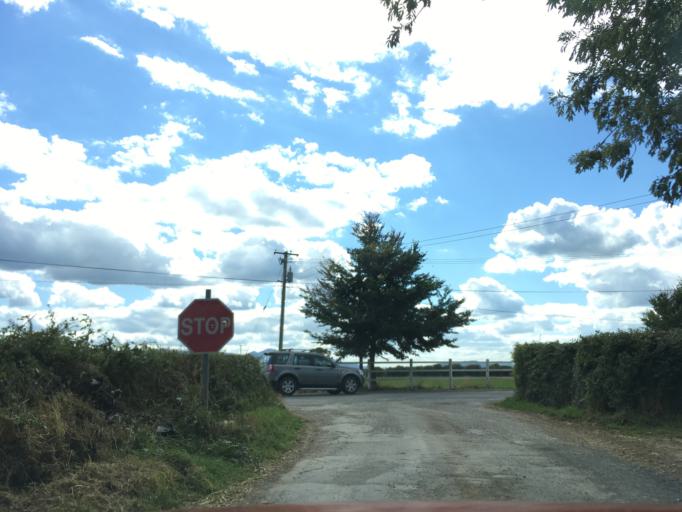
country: IE
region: Munster
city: Cashel
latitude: 52.4888
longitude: -7.9533
